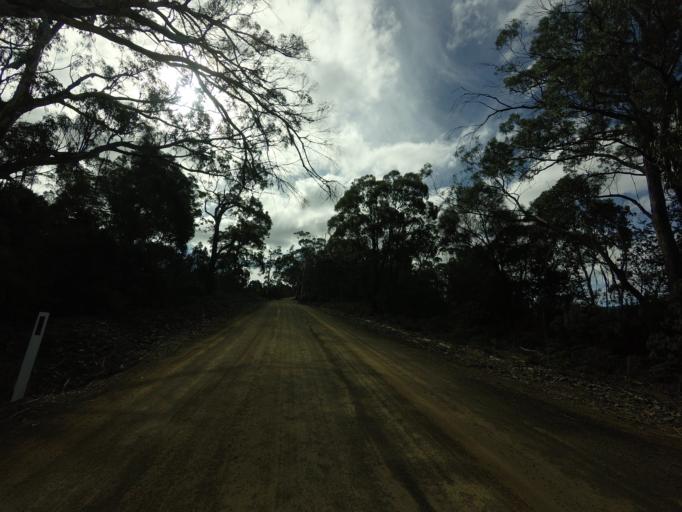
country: AU
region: Tasmania
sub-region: Clarence
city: Sandford
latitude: -43.0956
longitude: 147.7217
